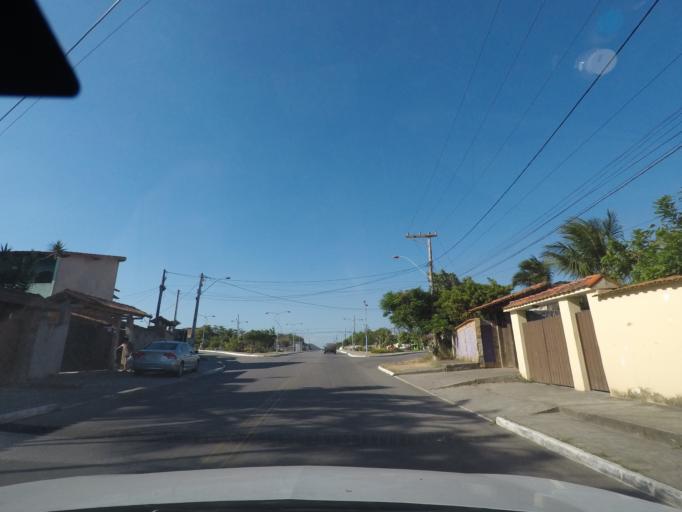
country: BR
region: Rio de Janeiro
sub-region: Marica
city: Marica
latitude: -22.9703
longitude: -42.9271
